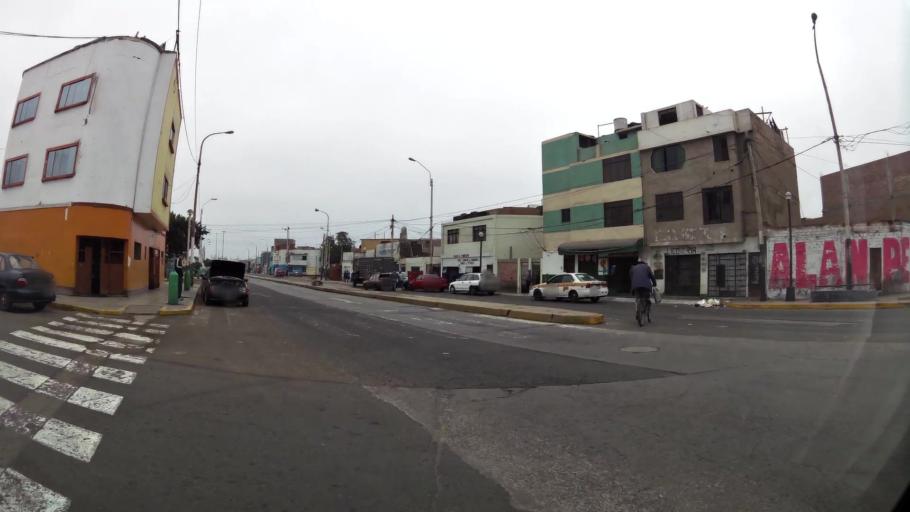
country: PE
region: Callao
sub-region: Callao
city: Callao
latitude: -12.0676
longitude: -77.1310
